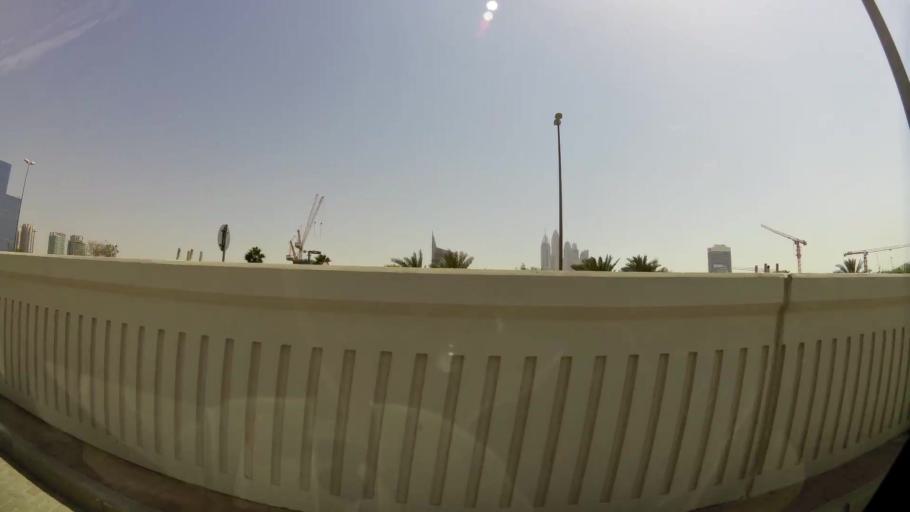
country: AE
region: Dubai
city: Dubai
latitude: 25.0998
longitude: 55.1674
